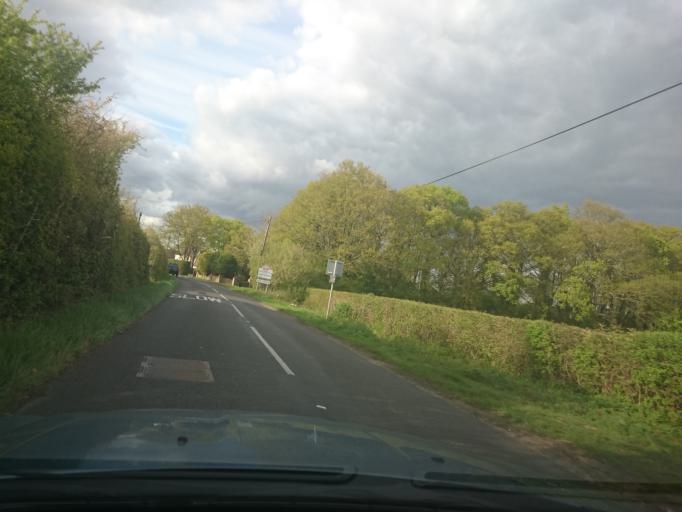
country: GB
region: England
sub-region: Surrey
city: Seale
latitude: 51.2350
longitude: -0.7082
